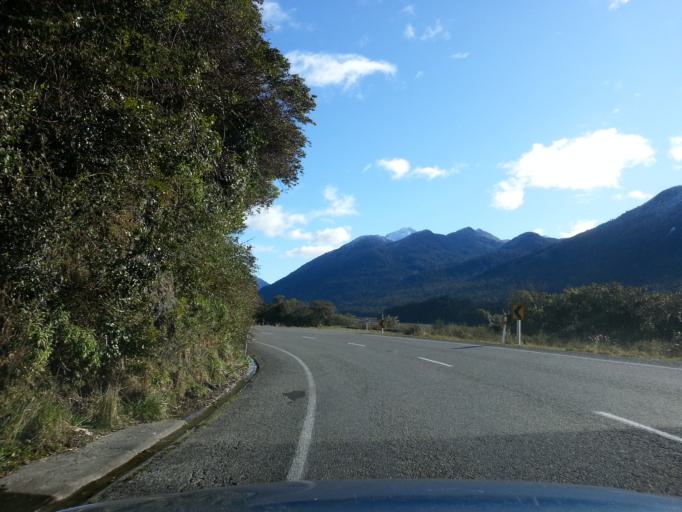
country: NZ
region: West Coast
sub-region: Grey District
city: Greymouth
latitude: -42.7337
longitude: 171.4469
